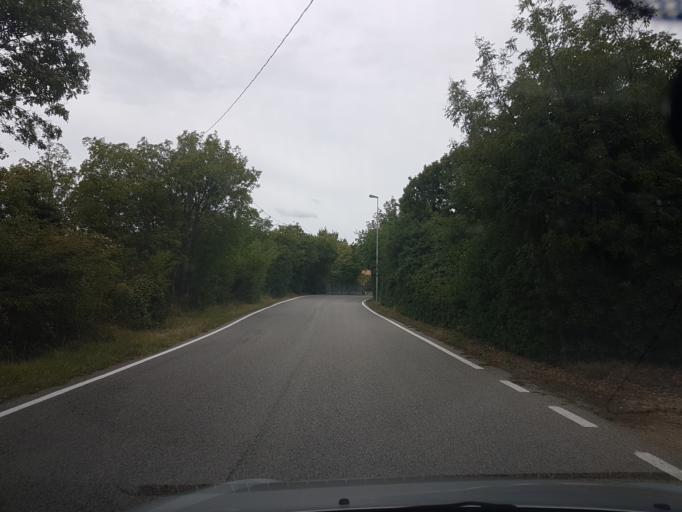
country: IT
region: Friuli Venezia Giulia
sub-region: Provincia di Trieste
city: Aurisina
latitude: 45.7593
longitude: 13.6877
